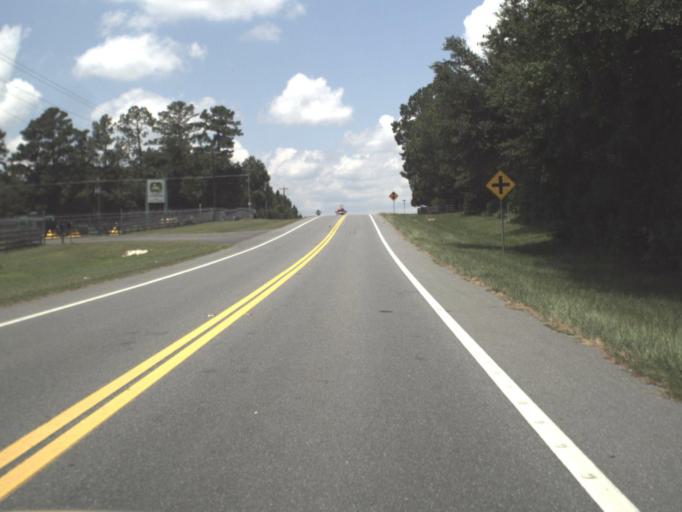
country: US
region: Florida
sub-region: Alachua County
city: High Springs
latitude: 30.0039
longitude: -82.5906
